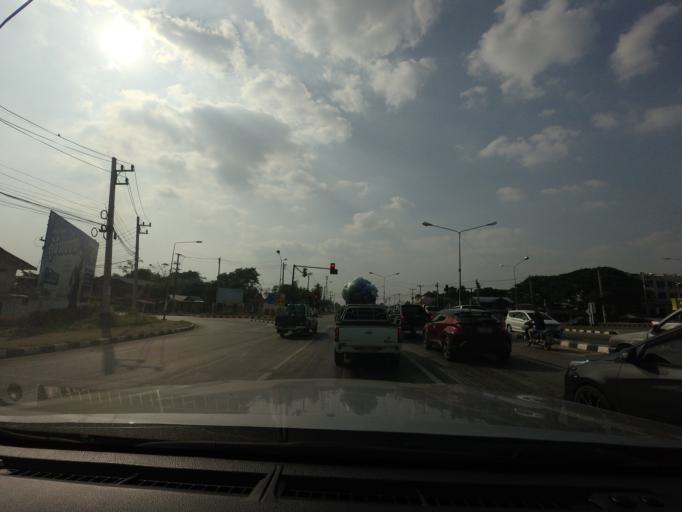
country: TH
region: Sukhothai
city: Sukhothai
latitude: 17.0261
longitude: 99.8823
